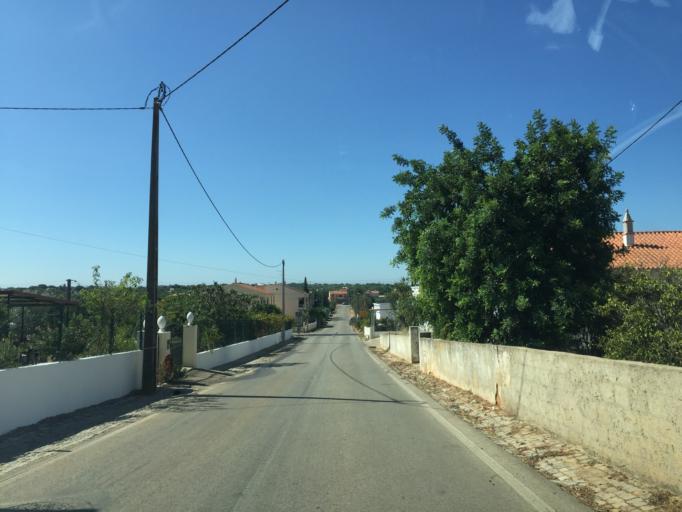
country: PT
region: Faro
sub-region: Loule
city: Vilamoura
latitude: 37.1144
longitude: -8.0997
